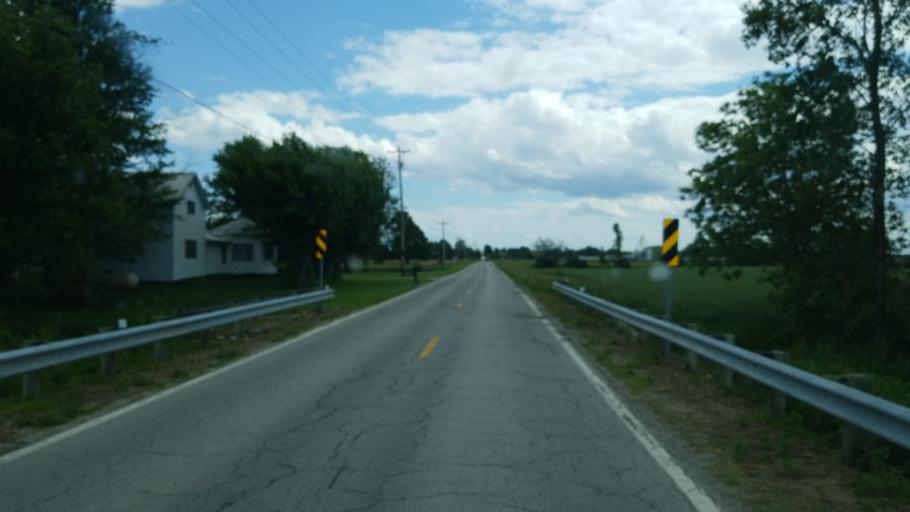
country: US
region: Ohio
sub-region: Huron County
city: Plymouth
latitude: 41.0631
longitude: -82.6102
